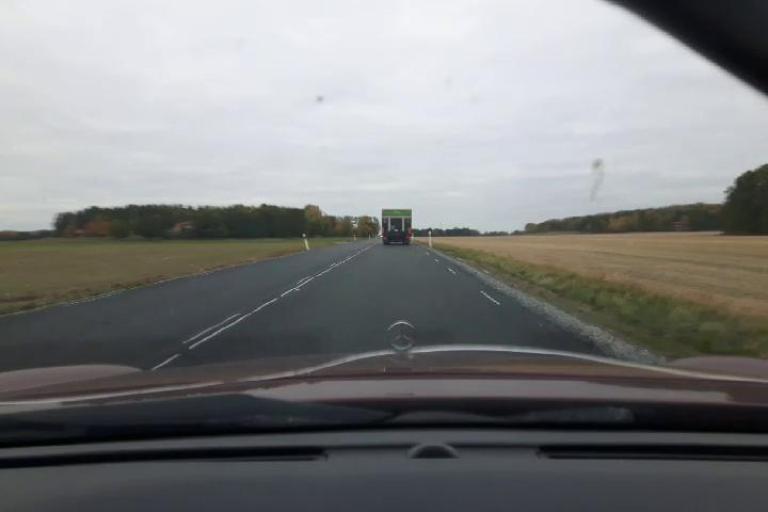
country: SE
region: Uppsala
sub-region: Enkopings Kommun
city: Enkoping
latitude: 59.6017
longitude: 17.0196
